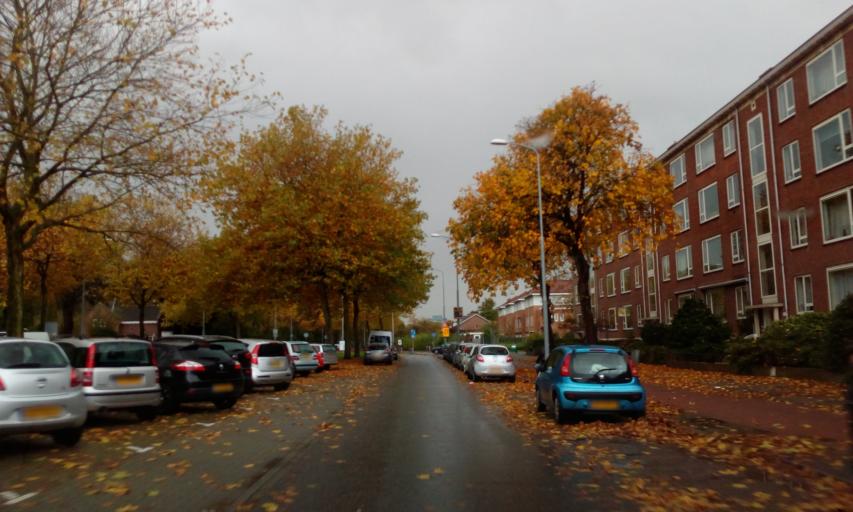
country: NL
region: South Holland
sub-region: Gemeente Rijswijk
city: Rijswijk
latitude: 52.0492
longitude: 4.3378
